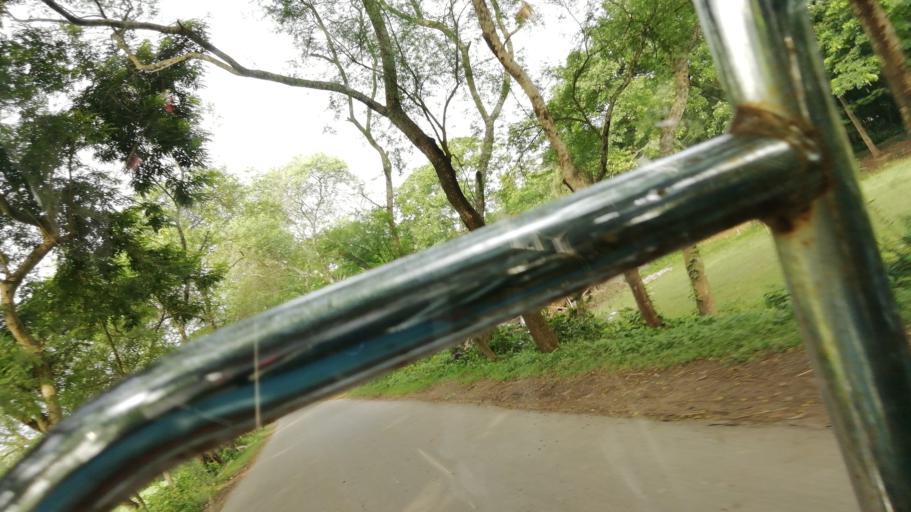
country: BD
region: Khulna
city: Kesabpur
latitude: 23.0286
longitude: 89.2677
